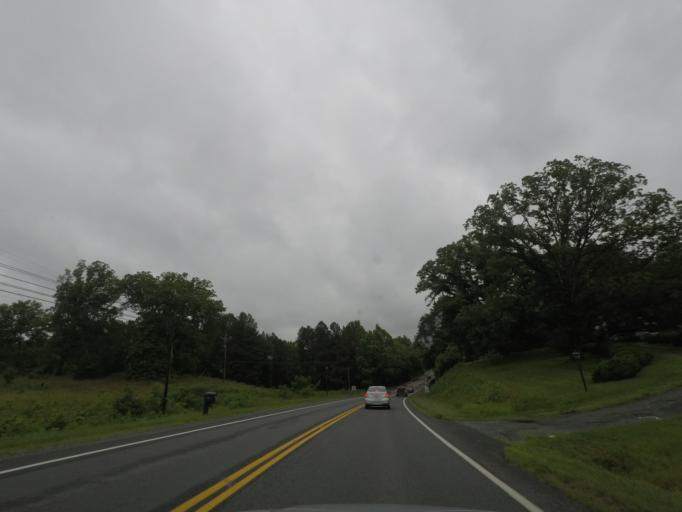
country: US
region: Virginia
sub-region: Fluvanna County
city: Palmyra
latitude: 37.8517
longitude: -78.2715
